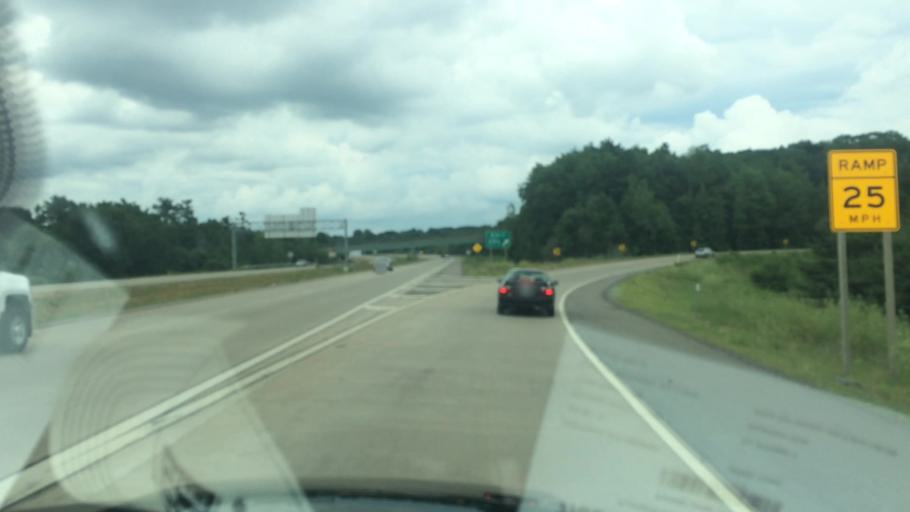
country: US
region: Wisconsin
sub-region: Marathon County
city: Rothschild
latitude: 44.8957
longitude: -89.6140
